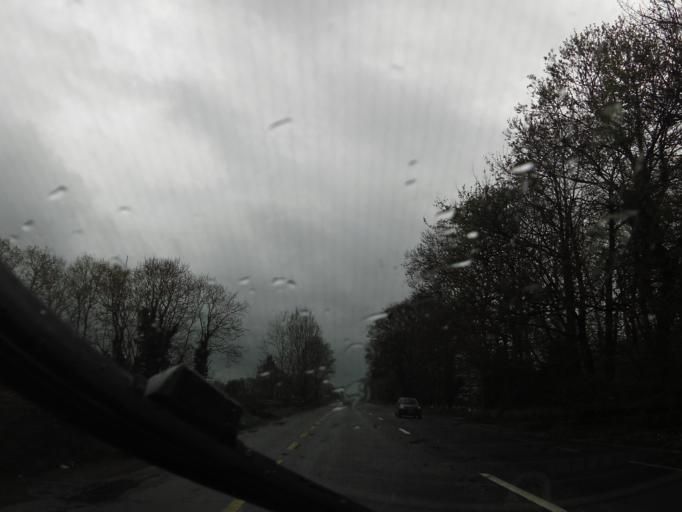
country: IE
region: Connaught
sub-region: County Galway
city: Claregalway
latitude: 53.3795
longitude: -8.9190
